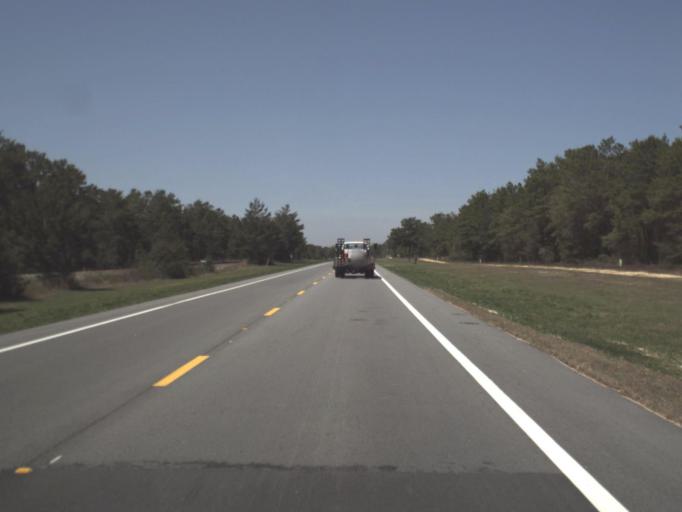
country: US
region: Florida
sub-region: Okaloosa County
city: Crestview
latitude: 30.7391
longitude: -86.3673
